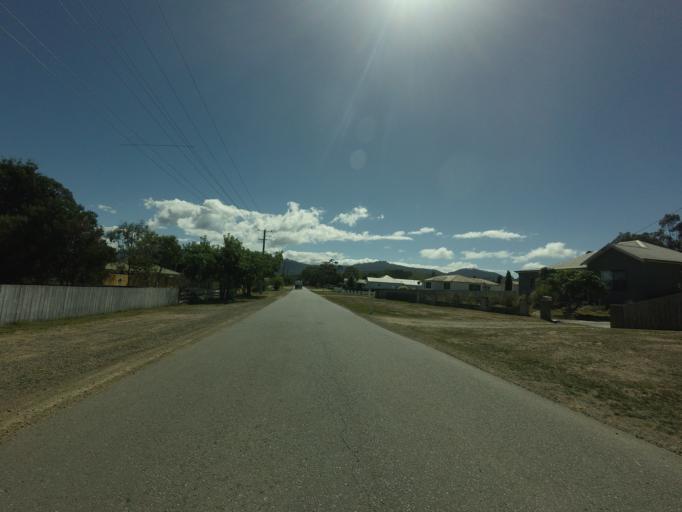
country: AU
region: Tasmania
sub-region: Break O'Day
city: St Helens
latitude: -41.5871
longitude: 148.1886
